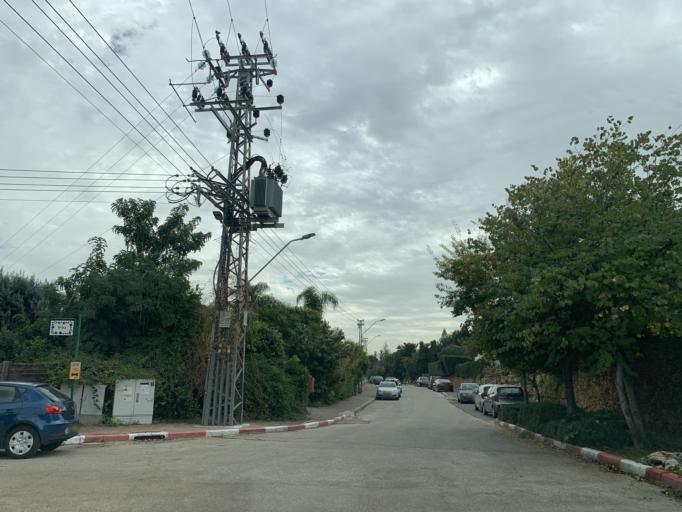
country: IL
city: Nirit
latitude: 32.1450
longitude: 34.9875
